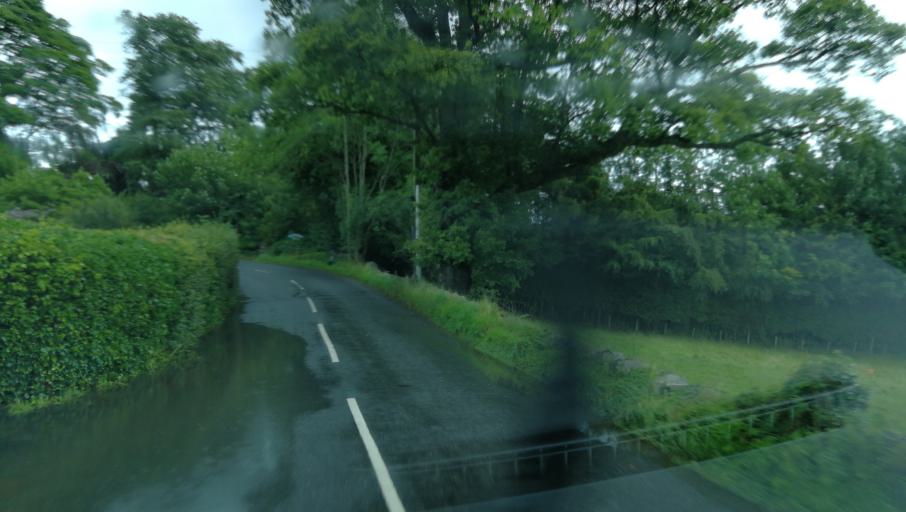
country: GB
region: England
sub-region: Cumbria
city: Penrith
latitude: 54.5935
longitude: -2.8589
